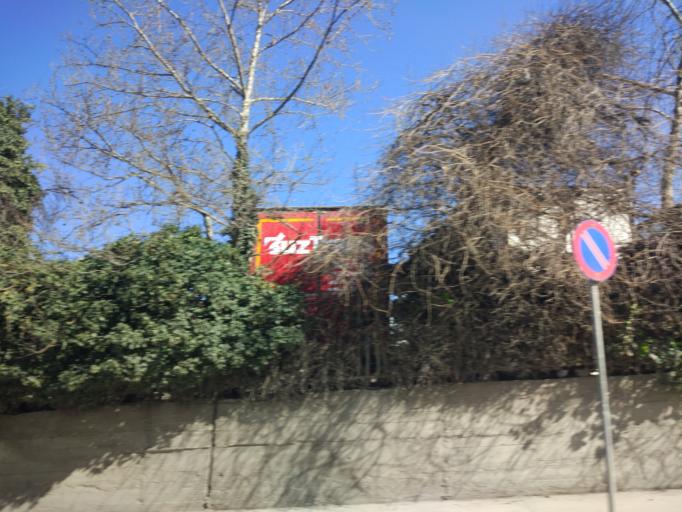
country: TR
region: Istanbul
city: Mahmutbey
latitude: 41.0259
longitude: 28.8072
